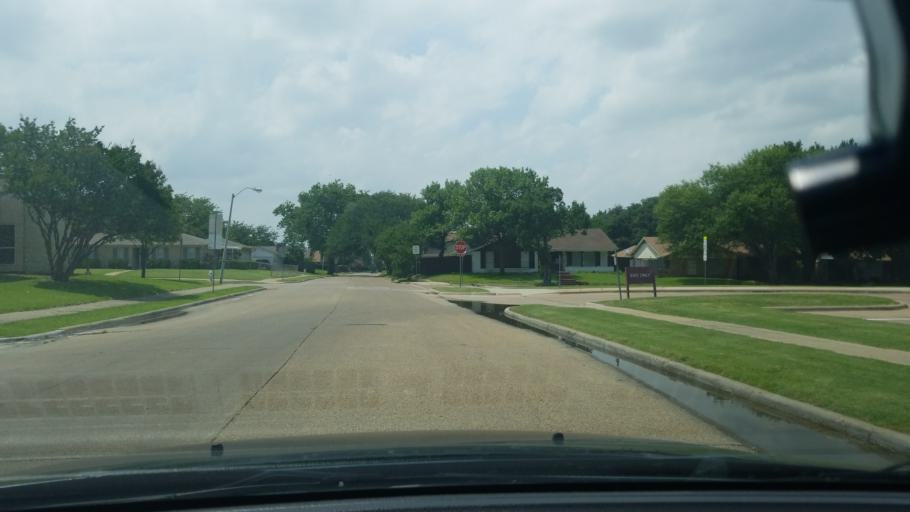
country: US
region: Texas
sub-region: Dallas County
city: Mesquite
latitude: 32.8087
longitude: -96.6445
